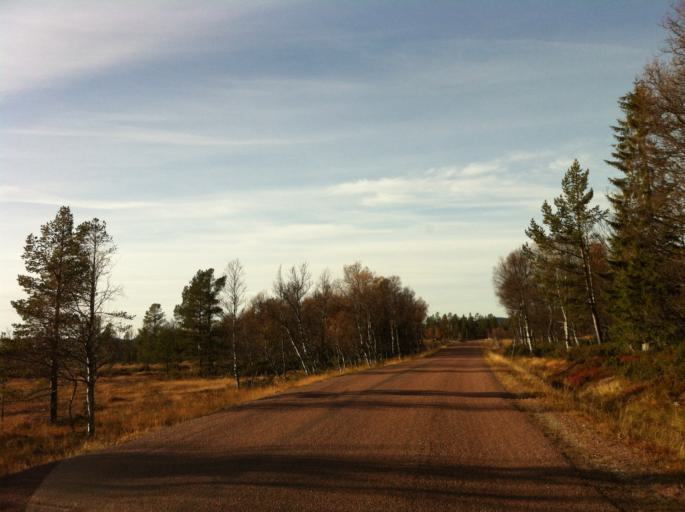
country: NO
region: Hedmark
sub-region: Engerdal
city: Engerdal
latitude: 62.0678
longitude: 12.2160
